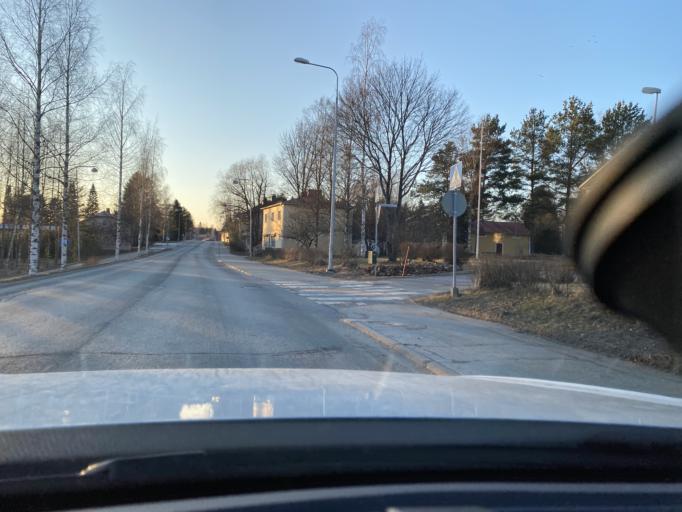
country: FI
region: Pirkanmaa
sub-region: Lounais-Pirkanmaa
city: Punkalaidun
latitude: 61.1159
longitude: 23.0914
